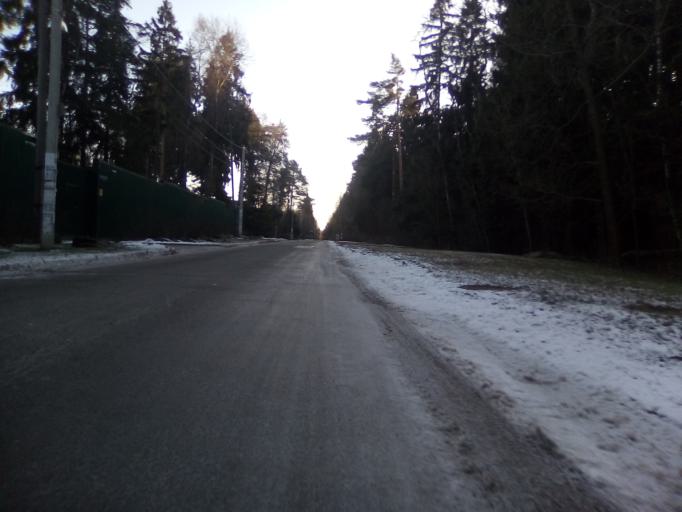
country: RU
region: Moskovskaya
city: Zhavoronki
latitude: 55.6400
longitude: 37.1453
